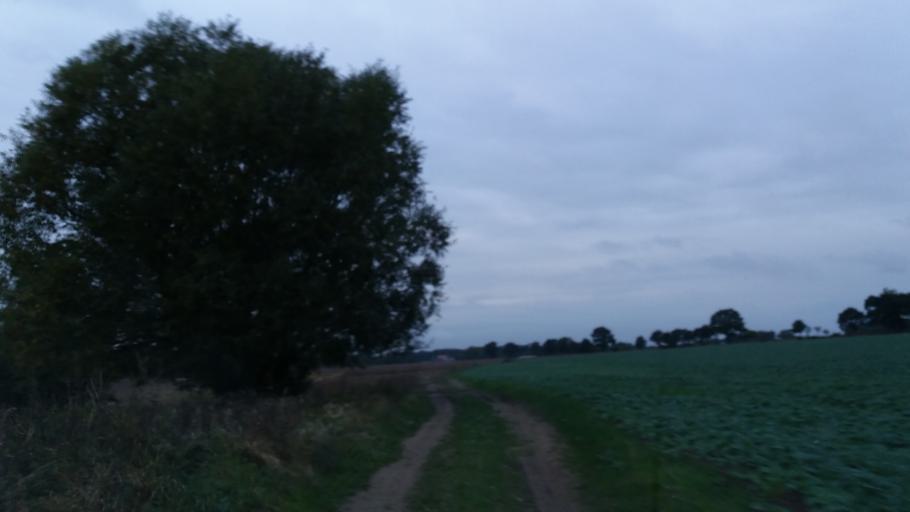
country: PL
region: West Pomeranian Voivodeship
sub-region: Powiat choszczenski
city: Krzecin
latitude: 53.0850
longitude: 15.4093
